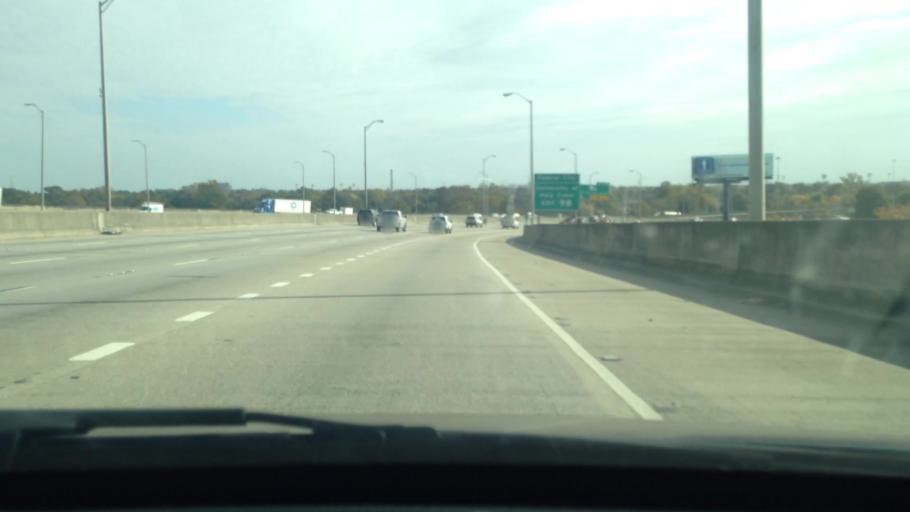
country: US
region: Louisiana
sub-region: Jefferson Parish
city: Gretna
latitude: 29.9378
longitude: -90.0430
